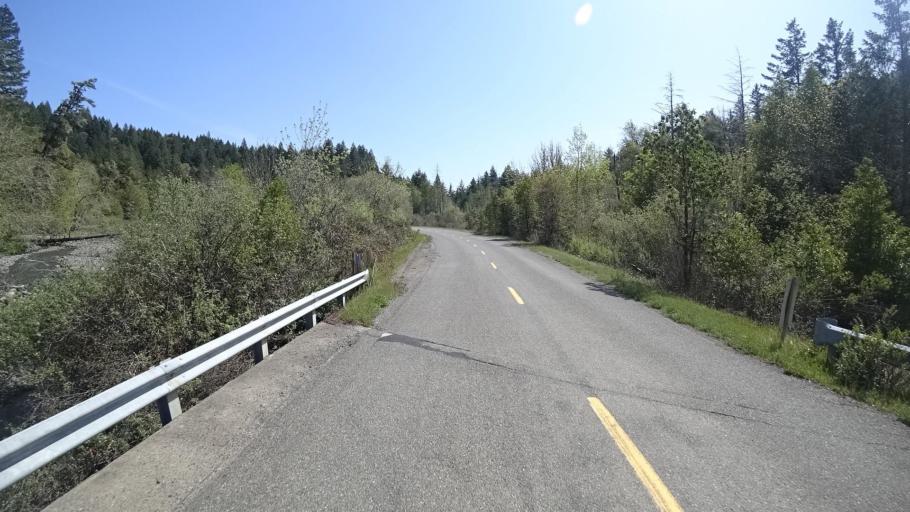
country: US
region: California
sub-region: Humboldt County
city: Redway
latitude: 40.3200
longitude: -123.6623
